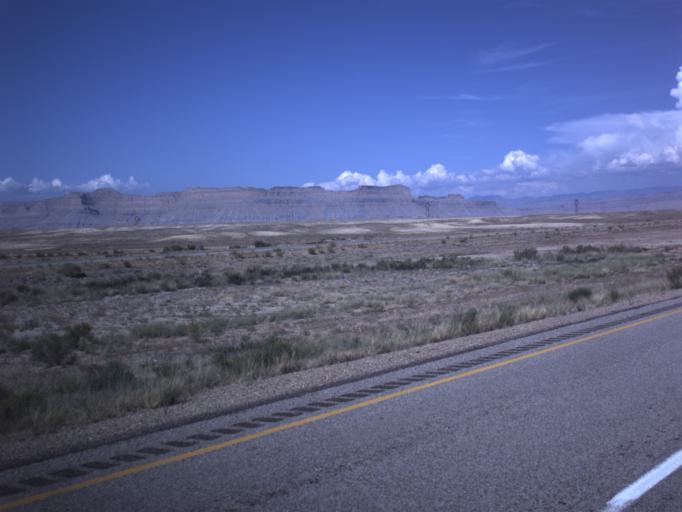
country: US
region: Utah
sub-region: Carbon County
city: East Carbon City
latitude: 38.9617
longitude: -110.2862
